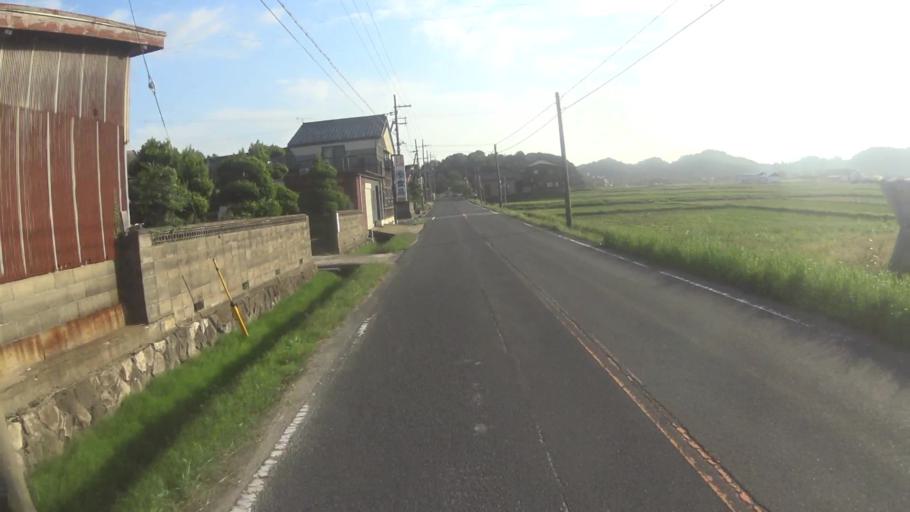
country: JP
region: Kyoto
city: Miyazu
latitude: 35.6667
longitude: 135.0914
